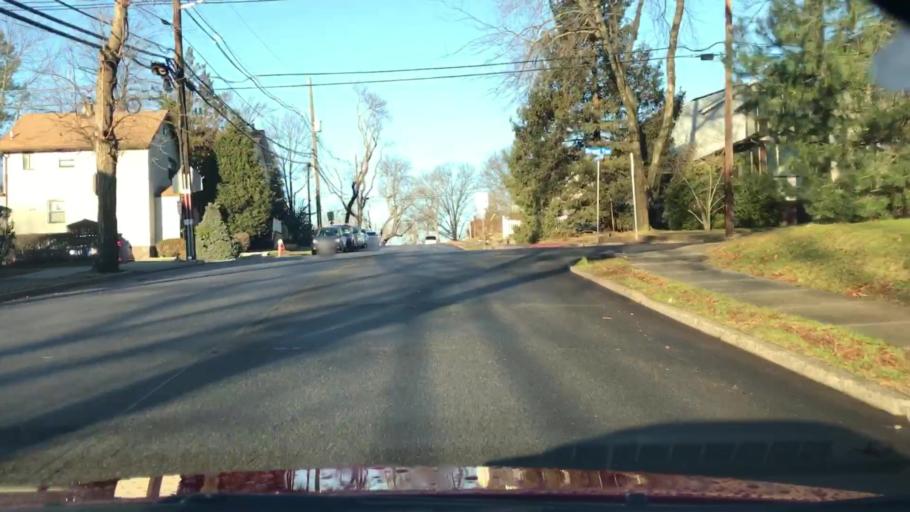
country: US
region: New Jersey
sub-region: Bergen County
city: Leonia
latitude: 40.8777
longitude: -74.0037
